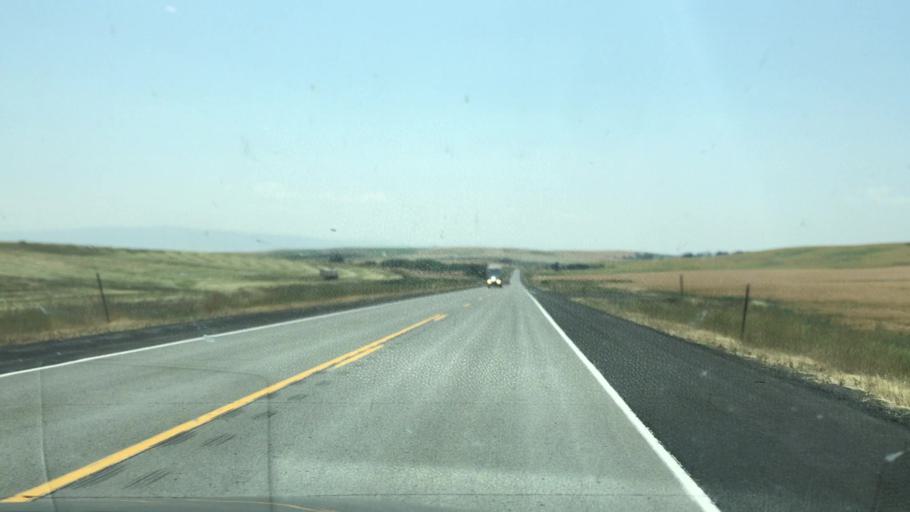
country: US
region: Idaho
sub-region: Lewis County
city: Nezperce
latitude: 46.0889
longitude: -116.3471
